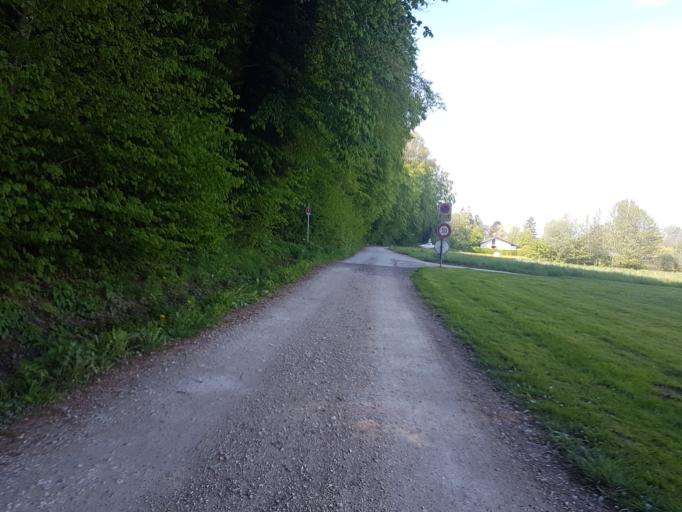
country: CH
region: Bern
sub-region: Seeland District
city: Tauffelen
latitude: 47.0480
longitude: 7.1620
